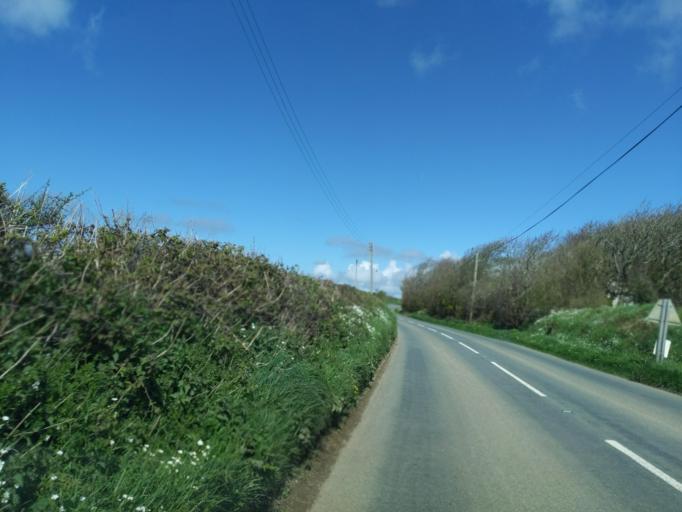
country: GB
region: England
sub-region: Cornwall
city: Wadebridge
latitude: 50.5828
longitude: -4.7880
